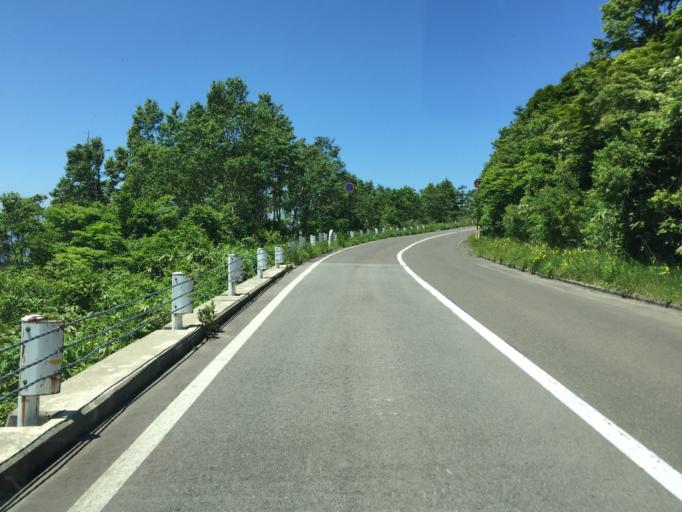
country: JP
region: Fukushima
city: Inawashiro
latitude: 37.6925
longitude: 140.2401
